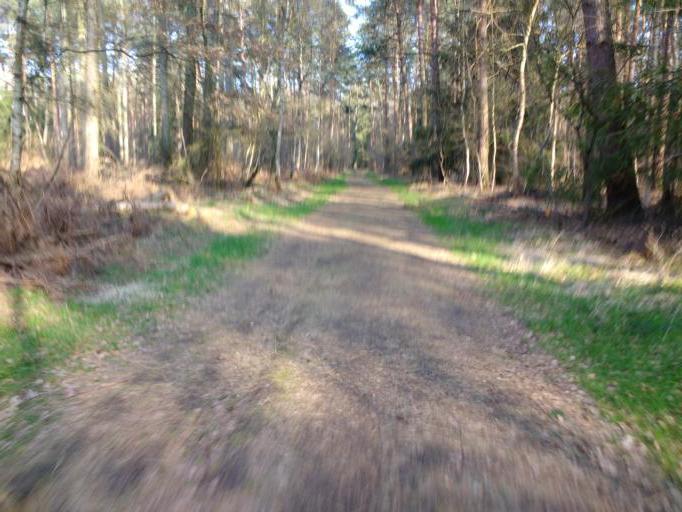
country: DE
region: Lower Saxony
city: Gifhorn
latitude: 52.4594
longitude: 10.5559
